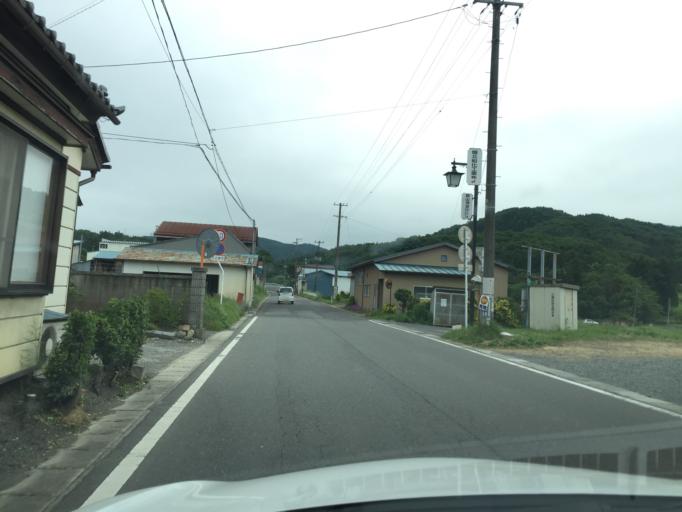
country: JP
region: Fukushima
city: Funehikimachi-funehiki
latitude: 37.3709
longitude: 140.6387
